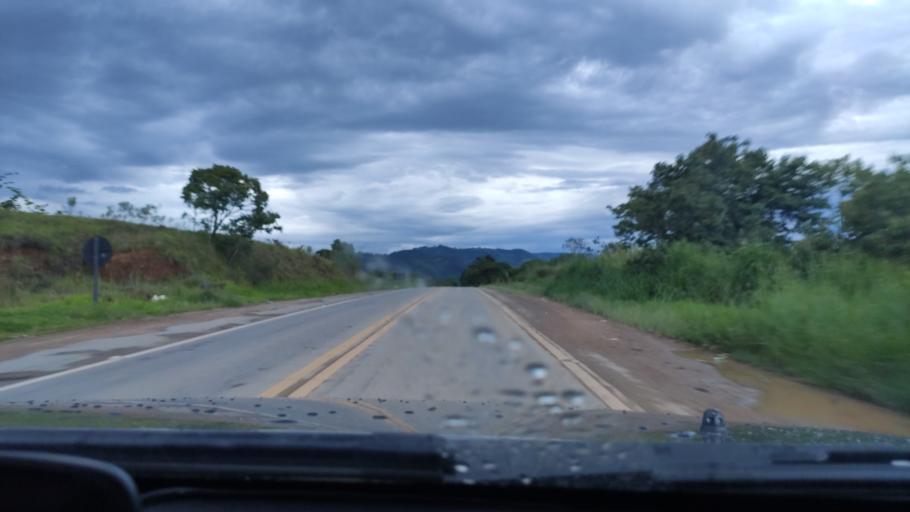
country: BR
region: Sao Paulo
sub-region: Socorro
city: Socorro
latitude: -22.7141
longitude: -46.5645
